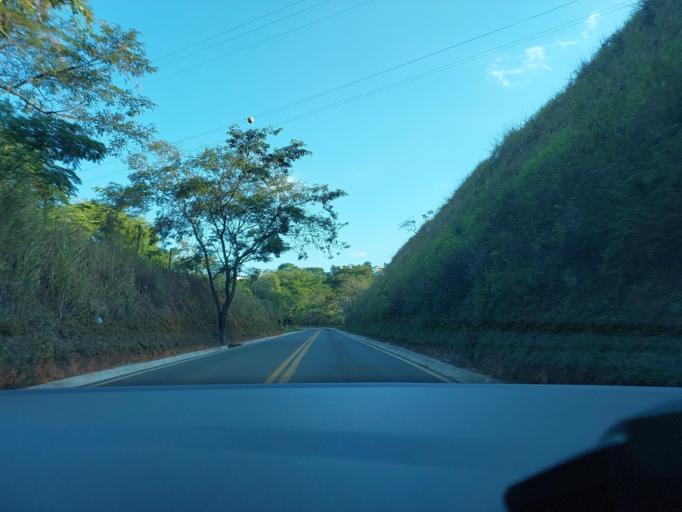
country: BR
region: Minas Gerais
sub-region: Muriae
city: Muriae
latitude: -21.1225
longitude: -42.4031
